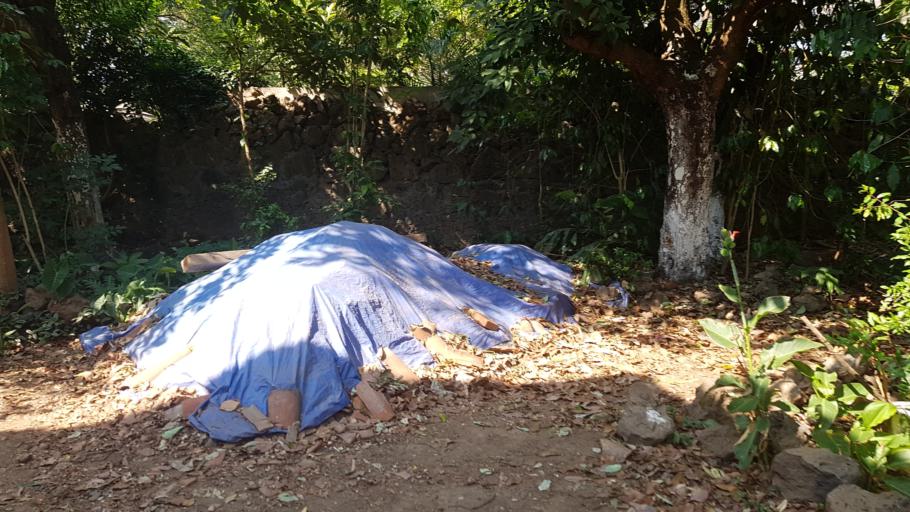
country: MX
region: Morelos
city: Tepoztlan
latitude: 18.9813
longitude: -99.0823
